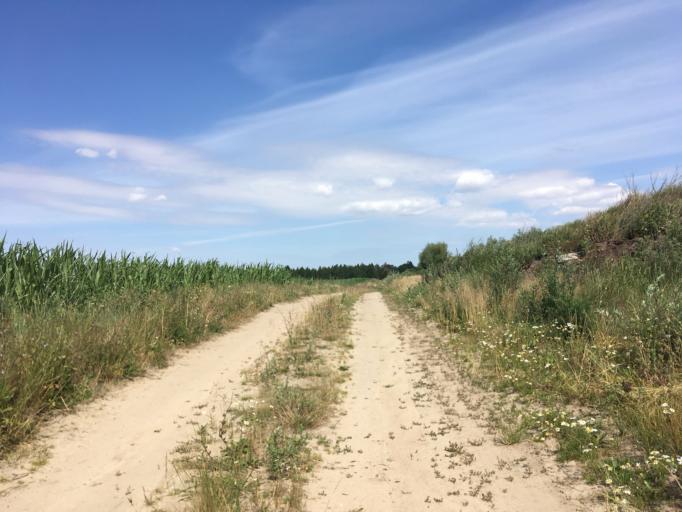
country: DE
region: Brandenburg
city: Casekow
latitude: 53.2239
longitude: 14.1384
